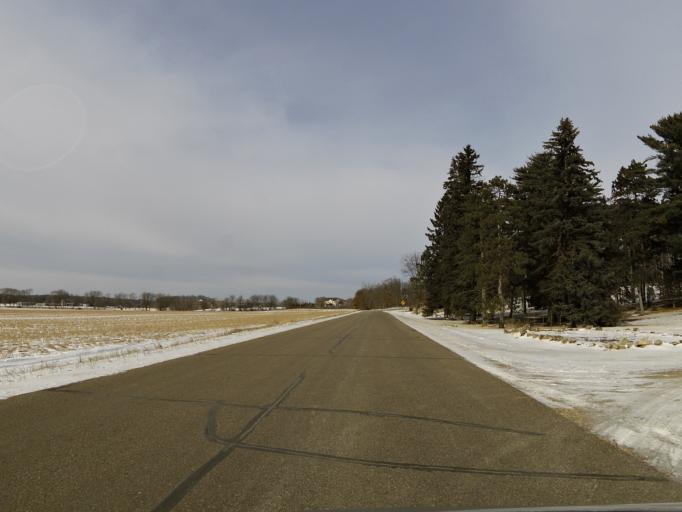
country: US
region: Minnesota
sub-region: Washington County
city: Stillwater
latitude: 45.0644
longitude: -92.7754
